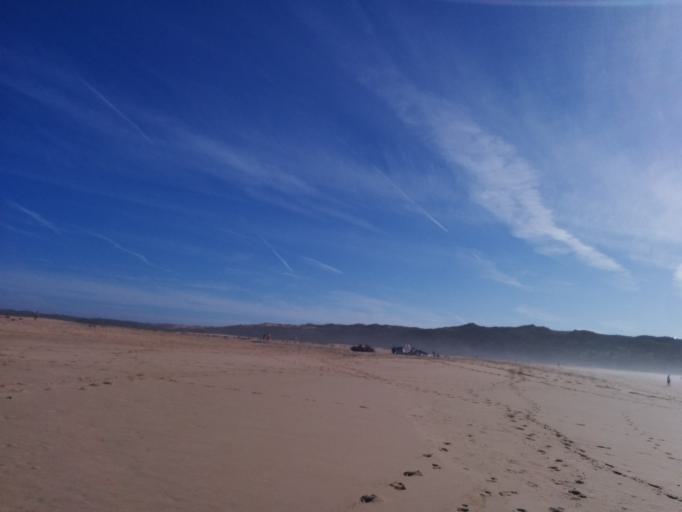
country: PT
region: Faro
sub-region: Vila do Bispo
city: Vila do Bispo
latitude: 37.2007
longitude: -8.9009
